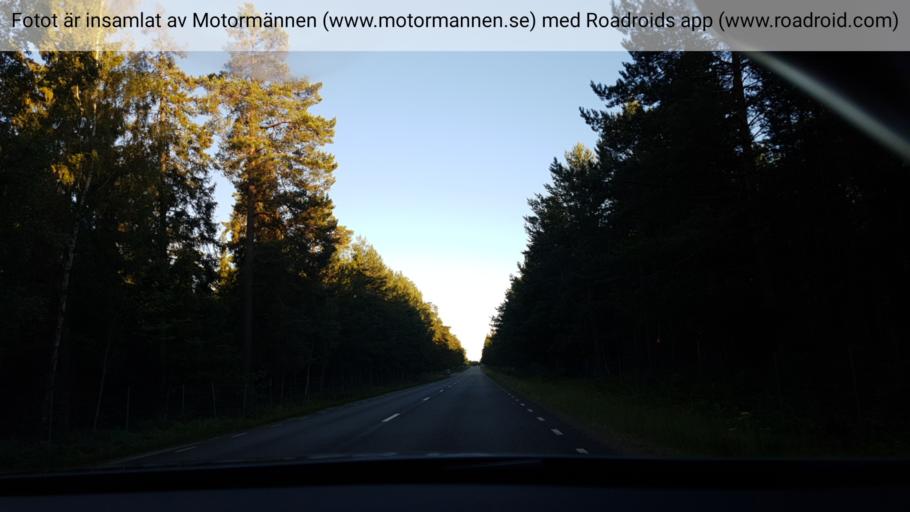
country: SE
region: Vaestra Goetaland
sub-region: Hjo Kommun
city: Hjo
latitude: 58.3716
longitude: 14.3518
